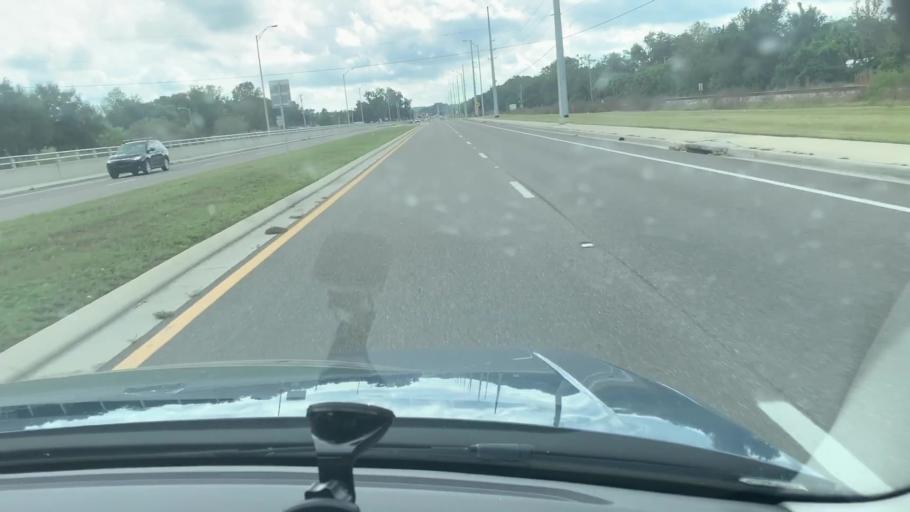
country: US
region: Florida
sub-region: Polk County
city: Kathleen
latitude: 28.1067
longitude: -82.0145
